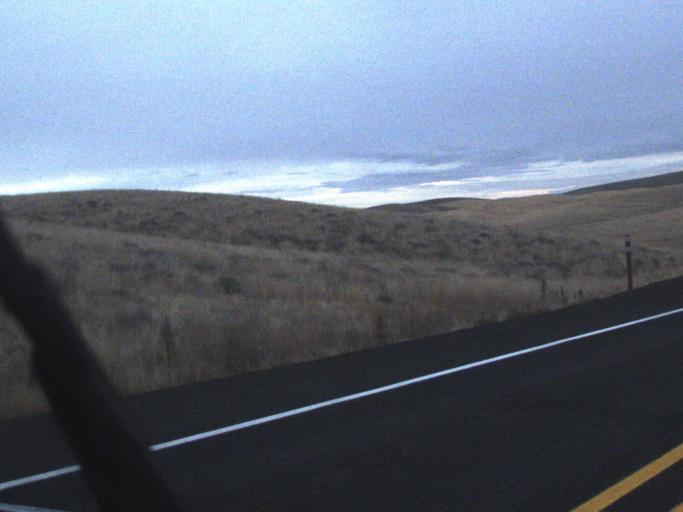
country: US
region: Washington
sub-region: Adams County
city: Ritzville
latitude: 46.7769
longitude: -118.3668
